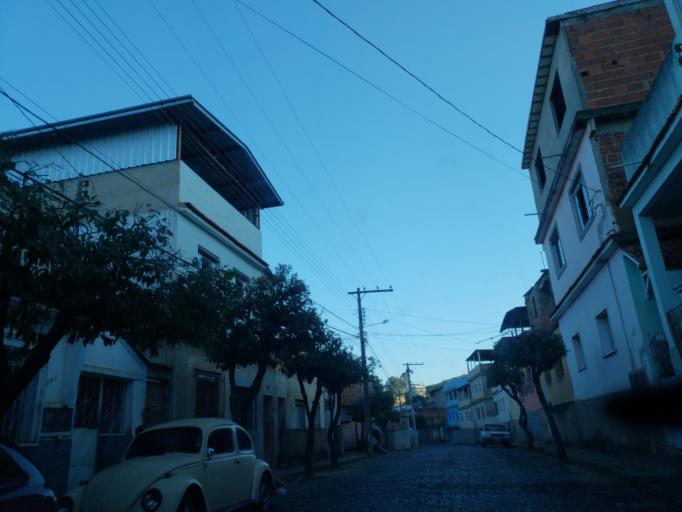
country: BR
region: Minas Gerais
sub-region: Sao Joao Nepomuceno
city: Sao Joao Nepomuceno
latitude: -21.5207
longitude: -43.0149
